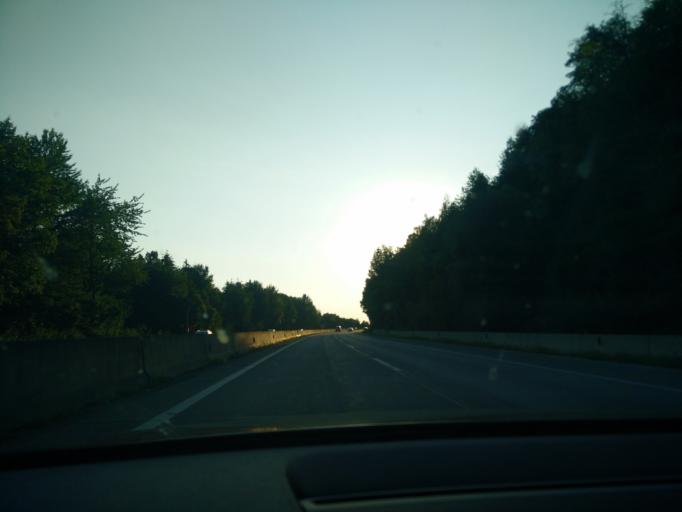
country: AT
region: Carinthia
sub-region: Klagenfurt am Woerthersee
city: Klagenfurt am Woerthersee
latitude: 46.6242
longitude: 14.2553
